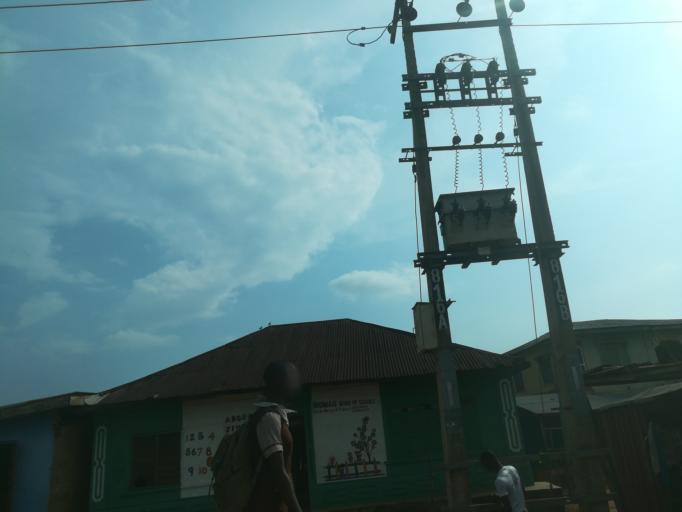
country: NG
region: Lagos
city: Ikorodu
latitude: 6.6659
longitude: 3.6698
